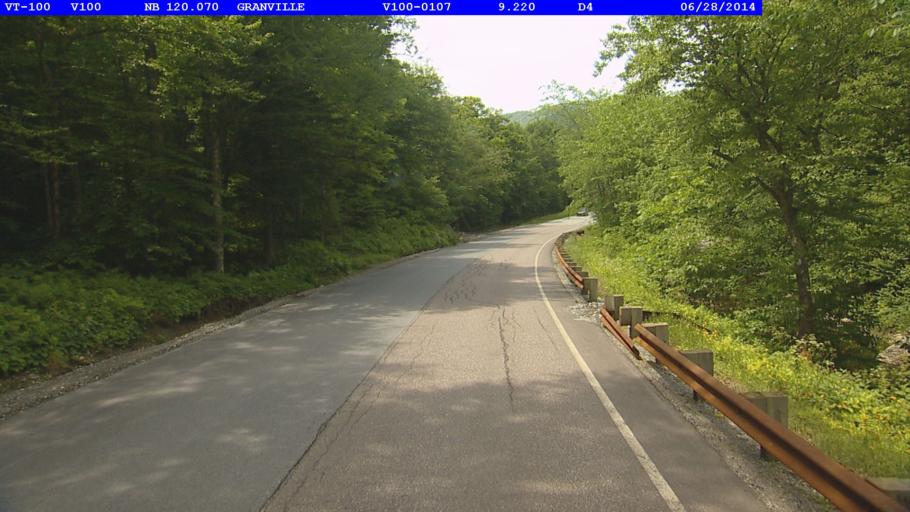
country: US
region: Vermont
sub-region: Washington County
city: Northfield
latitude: 44.0575
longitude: -72.8442
